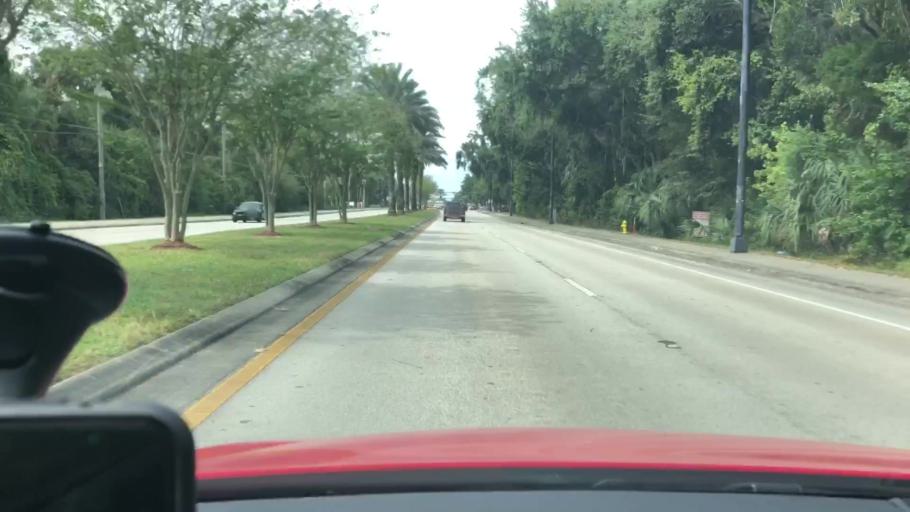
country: US
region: Florida
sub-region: Volusia County
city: Port Orange
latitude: 29.1221
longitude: -81.0020
